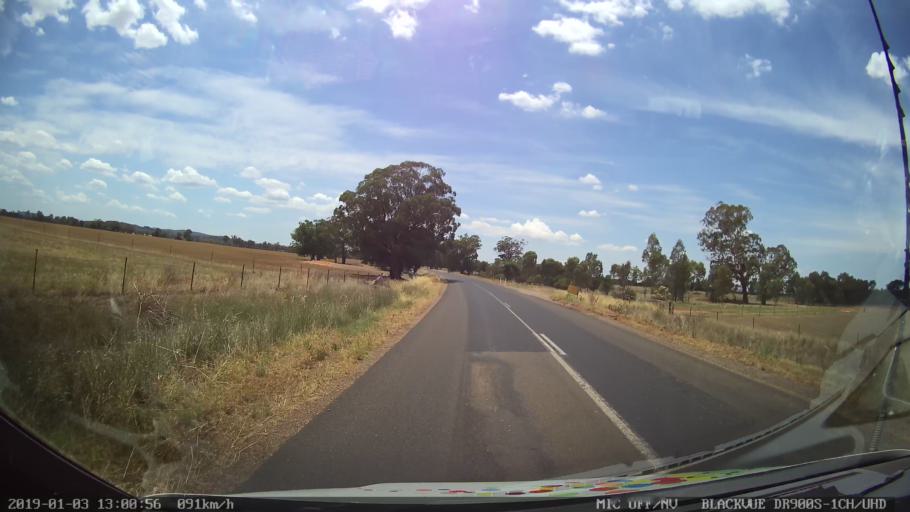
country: AU
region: New South Wales
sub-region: Cabonne
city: Canowindra
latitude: -33.6281
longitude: 148.4112
